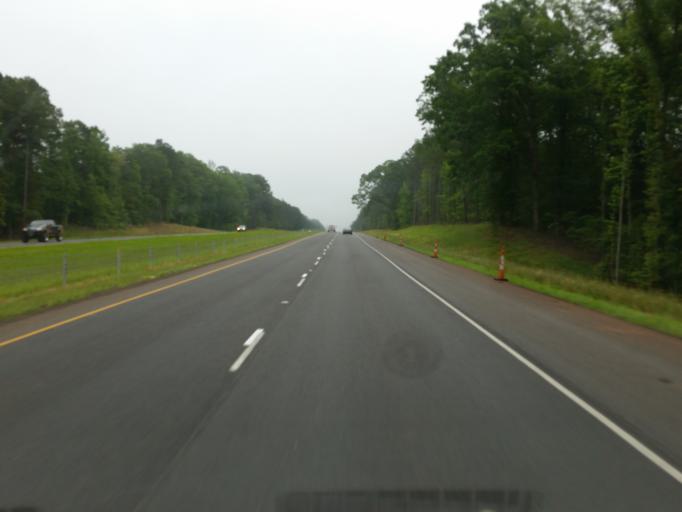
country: US
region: Louisiana
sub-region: Webster Parish
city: Minden
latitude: 32.5616
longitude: -93.1459
